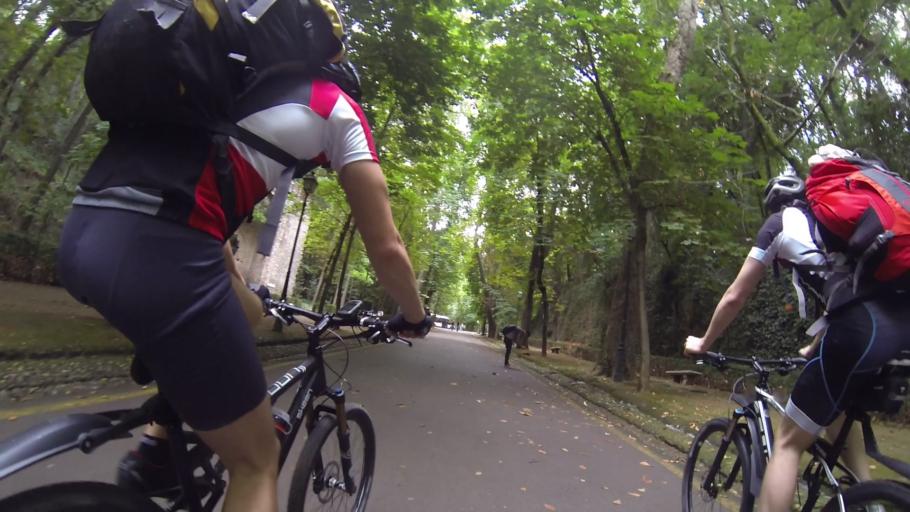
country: ES
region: Andalusia
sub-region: Provincia de Granada
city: Granada
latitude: 37.1755
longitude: -3.5899
